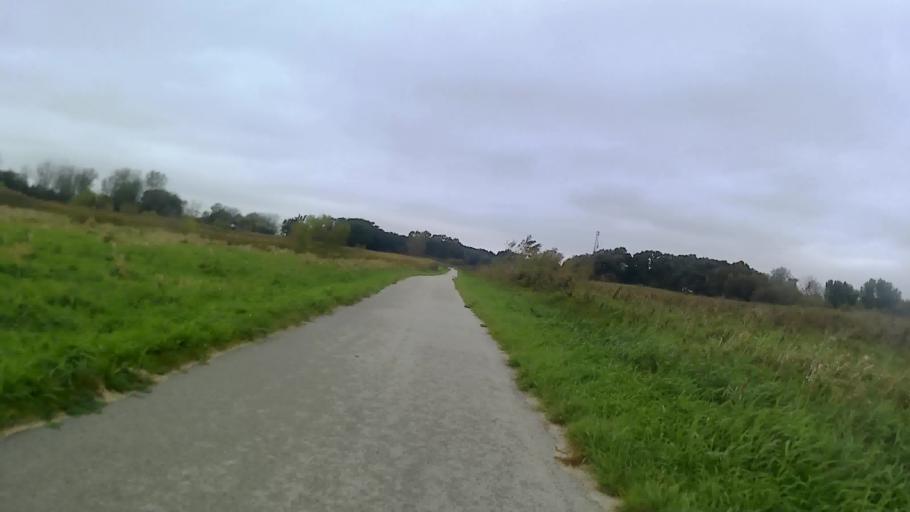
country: US
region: Illinois
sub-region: Kane County
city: Sugar Grove
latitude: 41.7924
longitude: -88.4534
